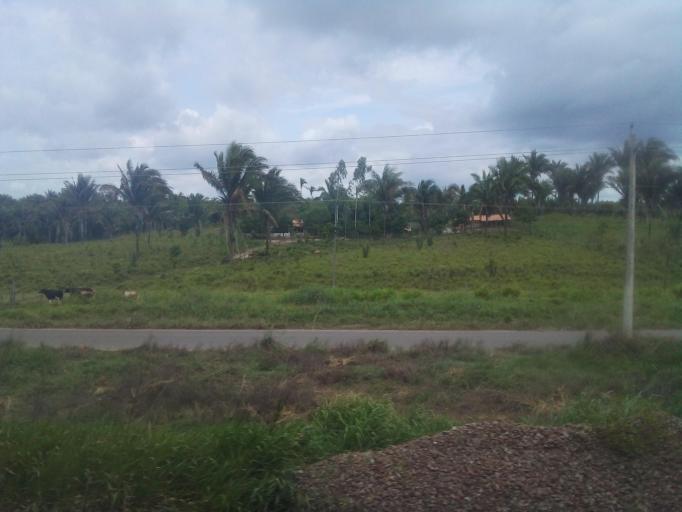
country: BR
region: Maranhao
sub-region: Santa Ines
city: Santa Ines
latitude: -3.7029
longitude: -45.9305
